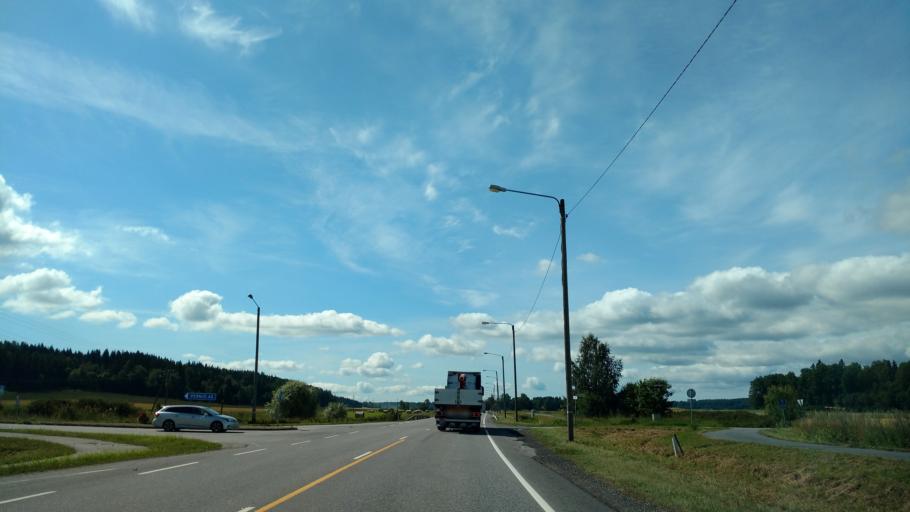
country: FI
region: Varsinais-Suomi
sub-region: Salo
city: Pernioe
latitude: 60.2510
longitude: 23.1342
